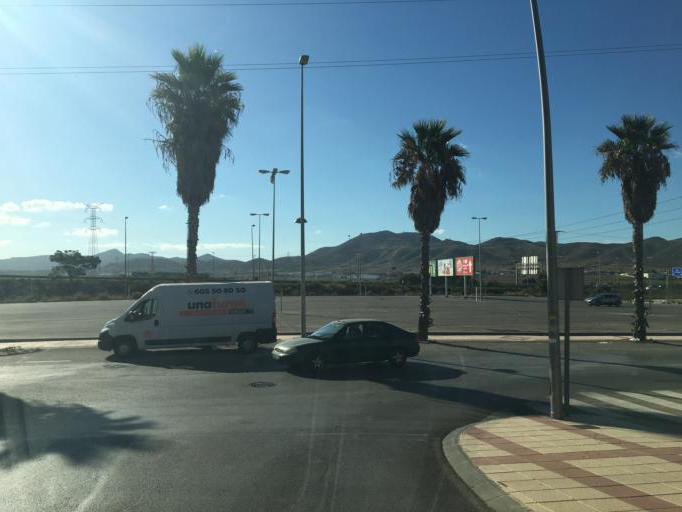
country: ES
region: Murcia
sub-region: Murcia
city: Cartagena
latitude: 37.6223
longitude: -0.9494
